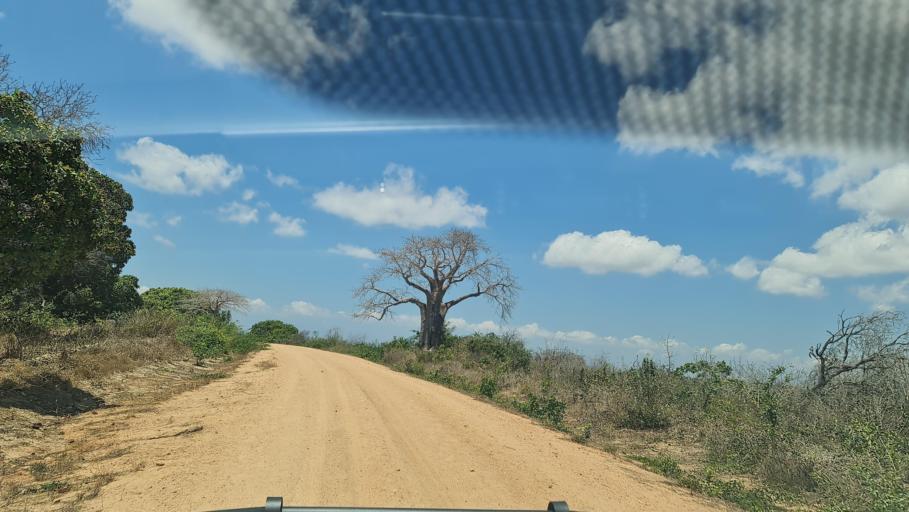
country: MZ
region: Nampula
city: Nacala
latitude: -14.3257
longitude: 40.5883
